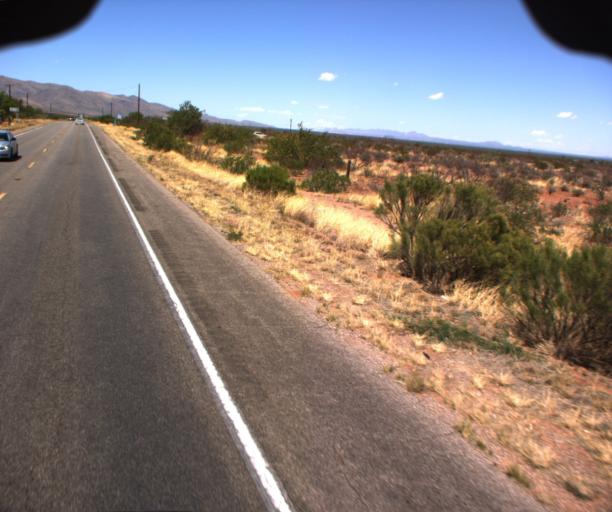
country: US
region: Arizona
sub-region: Cochise County
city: Bisbee
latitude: 31.3918
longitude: -109.7655
